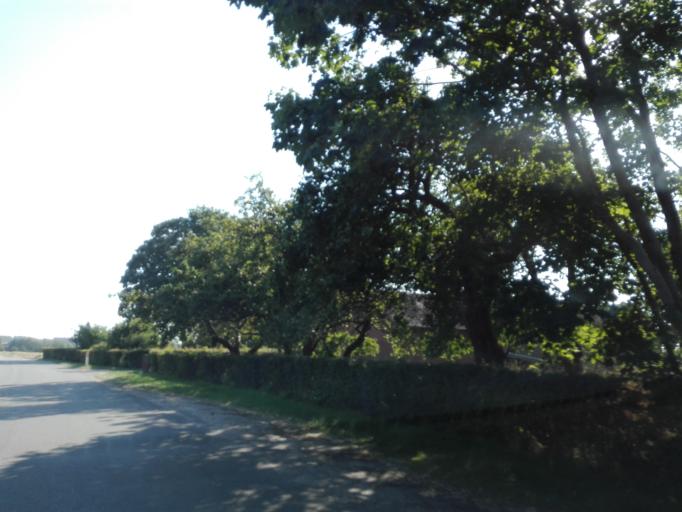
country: DK
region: Central Jutland
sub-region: Odder Kommune
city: Odder
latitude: 55.9376
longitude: 10.2356
